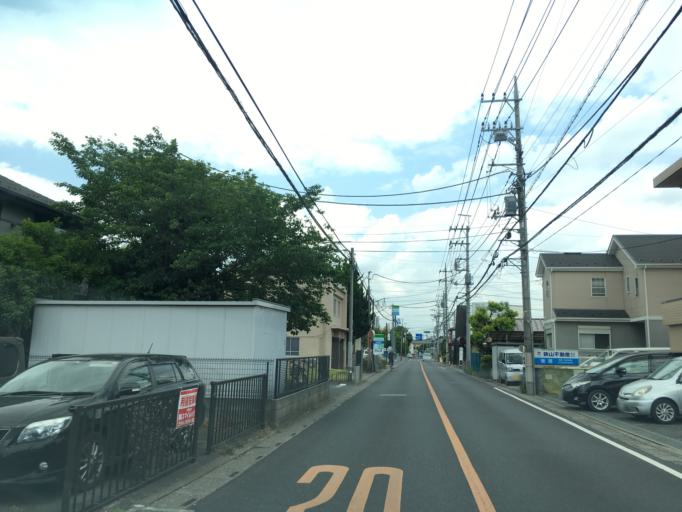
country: JP
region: Saitama
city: Sayama
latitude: 35.8674
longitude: 139.4206
